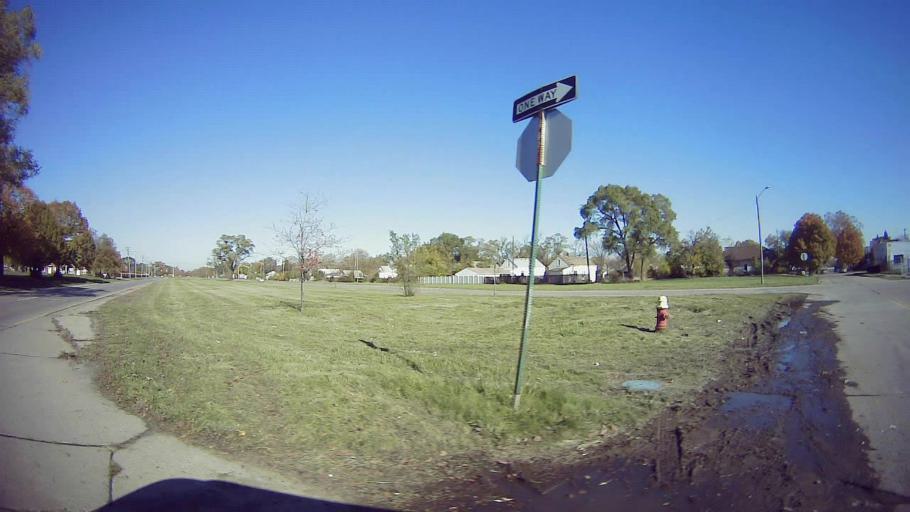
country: US
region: Michigan
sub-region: Wayne County
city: Hamtramck
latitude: 42.4089
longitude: -83.0430
